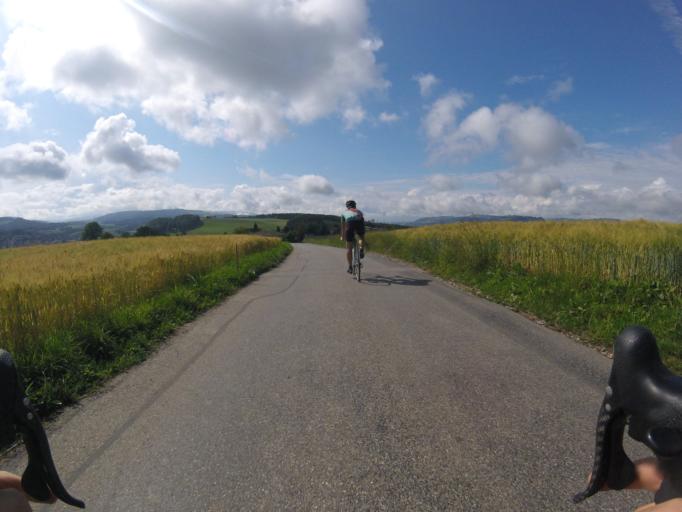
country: CH
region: Bern
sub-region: Bern-Mittelland District
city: Worb
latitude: 46.9345
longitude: 7.5445
